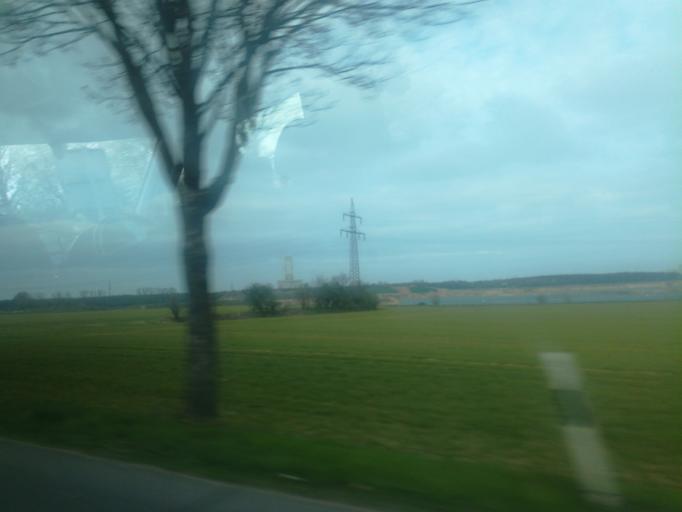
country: DE
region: North Rhine-Westphalia
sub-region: Regierungsbezirk Dusseldorf
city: Kamp-Lintfort
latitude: 51.5062
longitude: 6.5632
